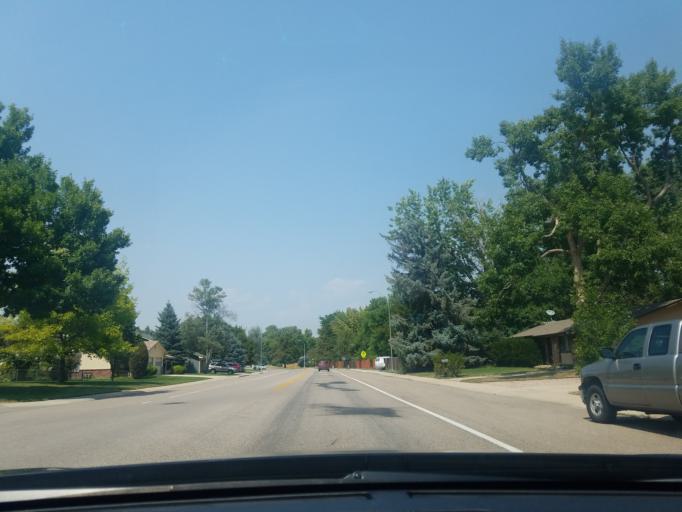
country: US
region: Colorado
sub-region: Larimer County
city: Fort Collins
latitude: 40.5484
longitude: -105.0671
